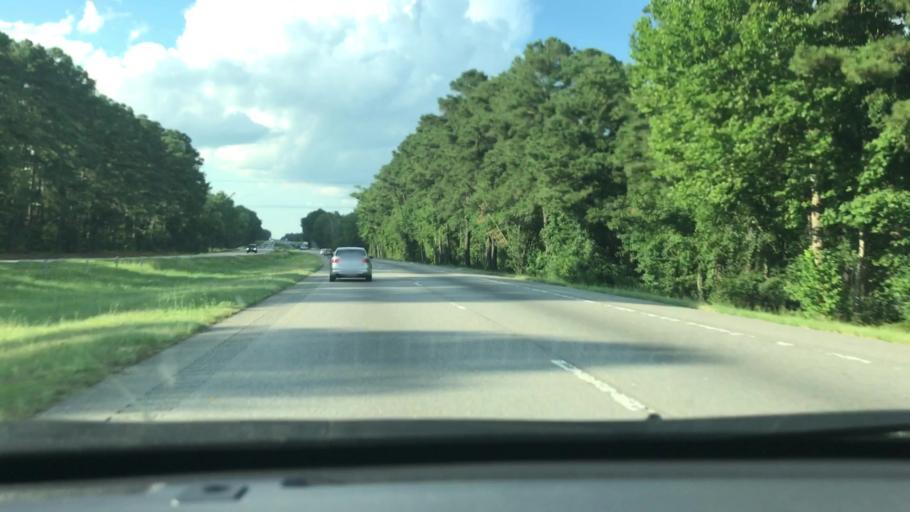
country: US
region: North Carolina
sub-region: Robeson County
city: Saint Pauls
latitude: 34.8549
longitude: -78.9664
